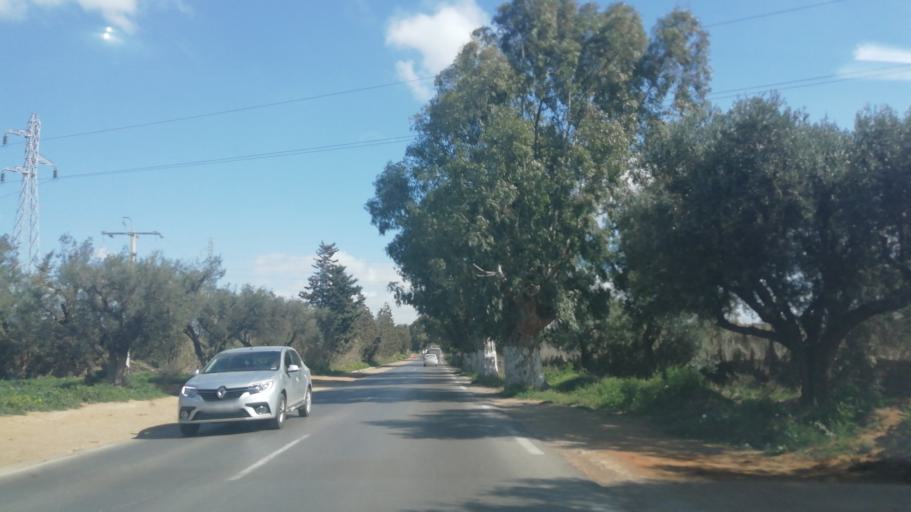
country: DZ
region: Mostaganem
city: Mostaganem
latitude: 35.9987
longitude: 0.3180
